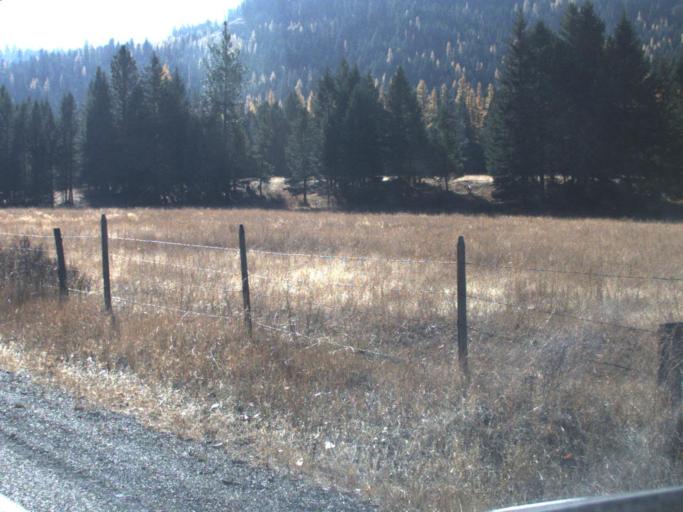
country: US
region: Washington
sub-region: Ferry County
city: Republic
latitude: 48.6038
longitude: -118.6560
